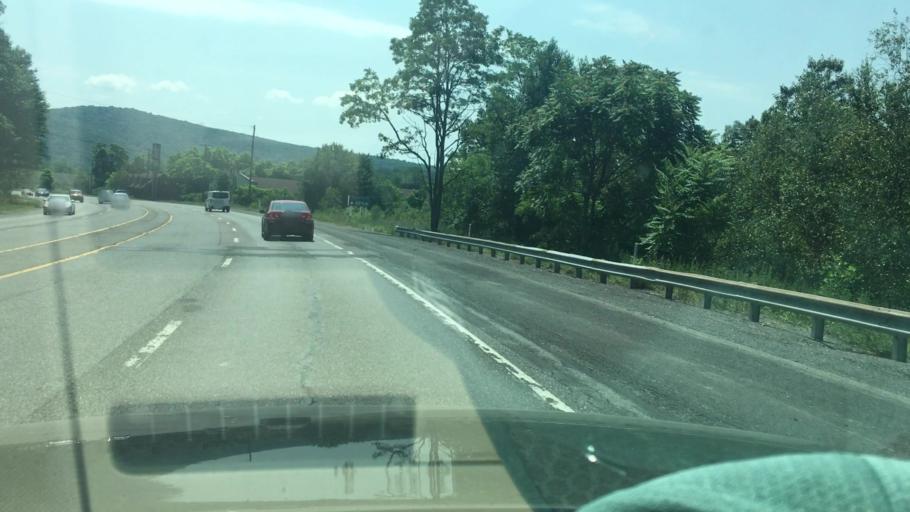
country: US
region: Pennsylvania
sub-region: Schuylkill County
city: Tamaqua
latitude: 40.7657
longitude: -75.9554
